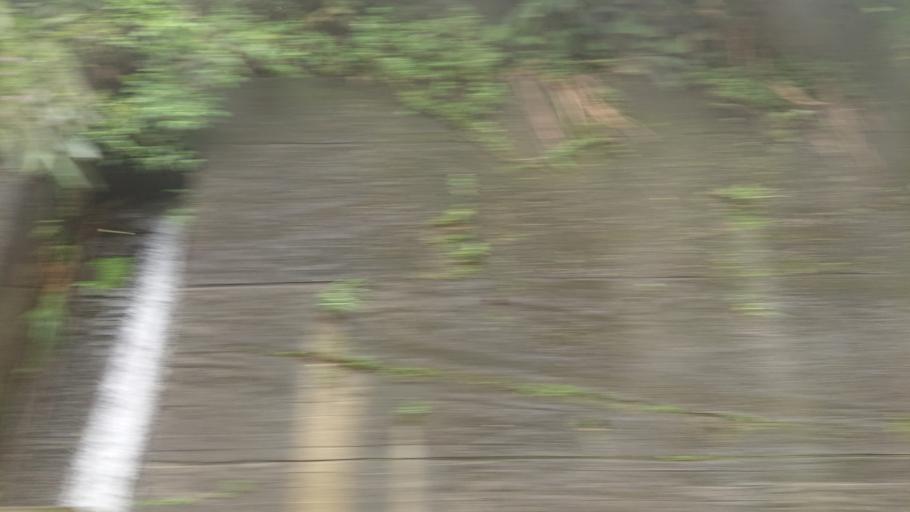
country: TW
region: Taiwan
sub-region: Keelung
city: Keelung
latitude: 25.0871
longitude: 121.7058
